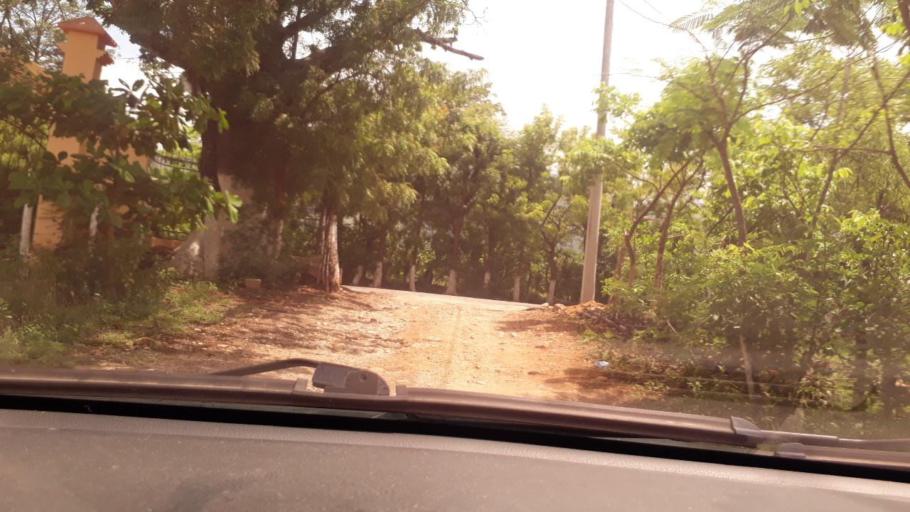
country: GT
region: Zacapa
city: Teculutan
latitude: 14.9945
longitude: -89.7254
